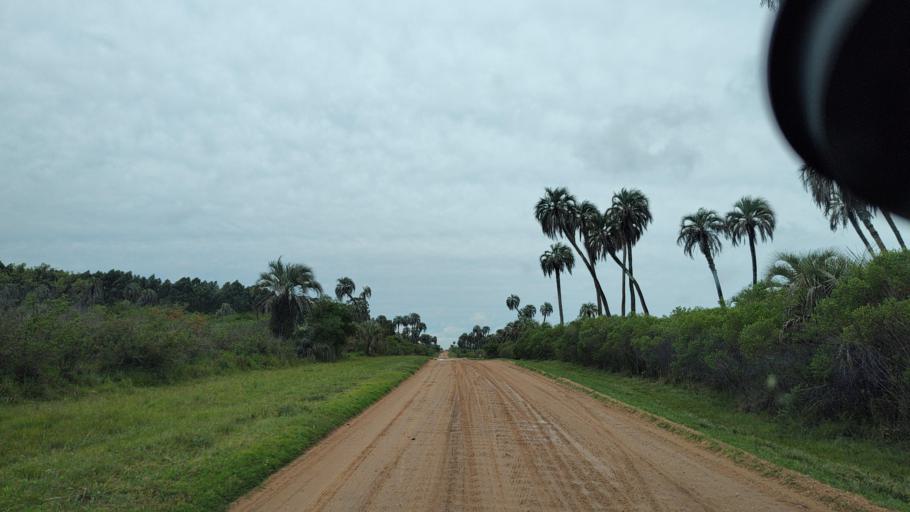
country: AR
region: Entre Rios
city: Ubajay
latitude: -31.8520
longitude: -58.2982
